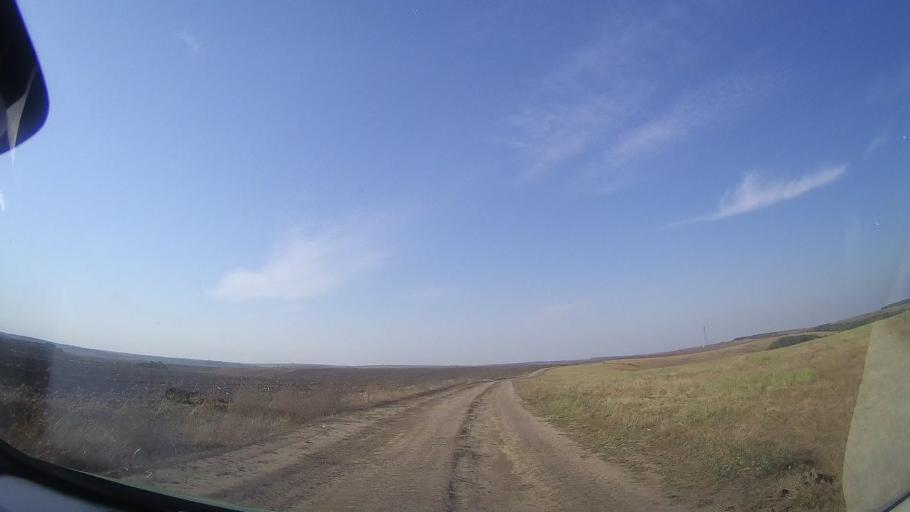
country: RO
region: Timis
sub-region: Comuna Bogda
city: Bogda
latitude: 45.8847
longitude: 21.5559
